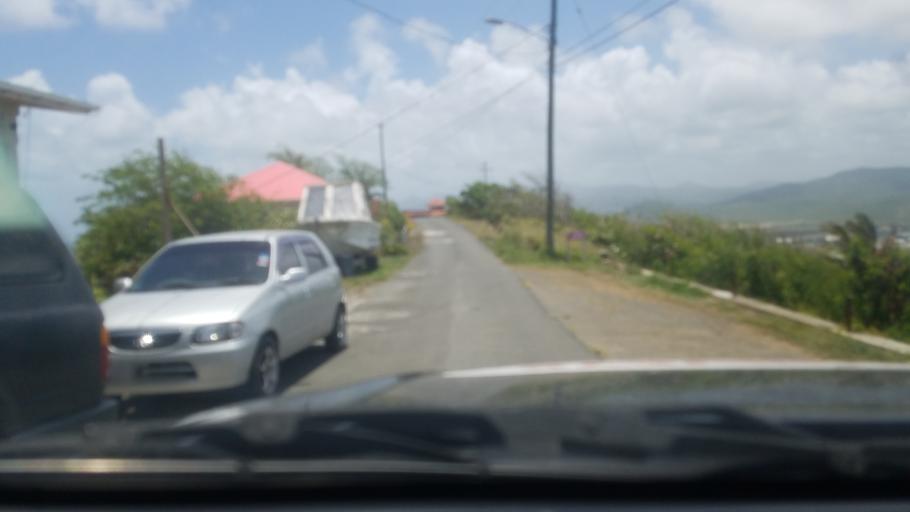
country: LC
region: Vieux-Fort
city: Vieux Fort
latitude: 13.7160
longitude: -60.9475
